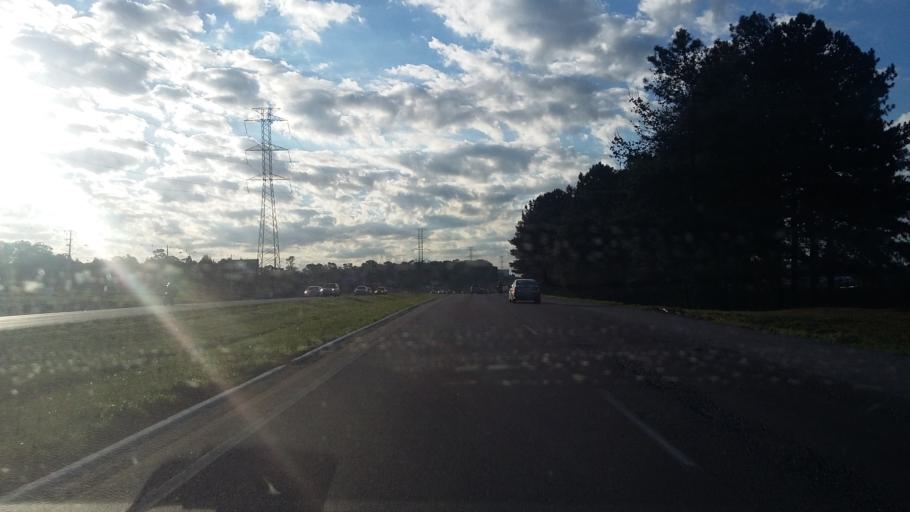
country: BR
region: Parana
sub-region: Curitiba
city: Curitiba
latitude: -25.4695
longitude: -49.3546
